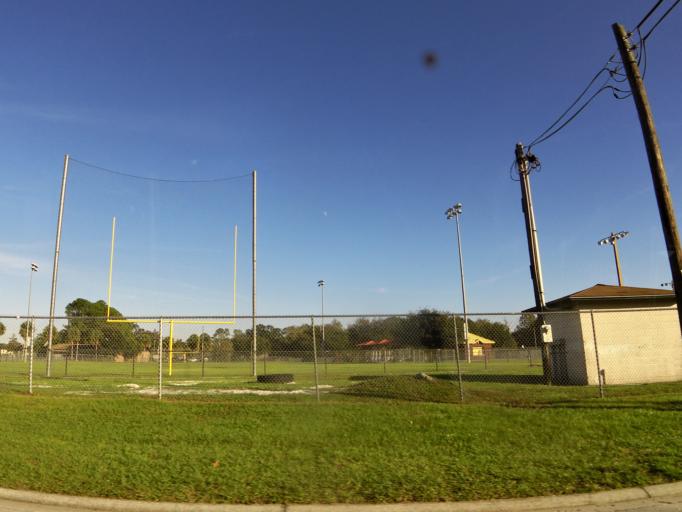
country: US
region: Florida
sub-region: Duval County
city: Jacksonville
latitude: 30.3556
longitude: -81.7039
